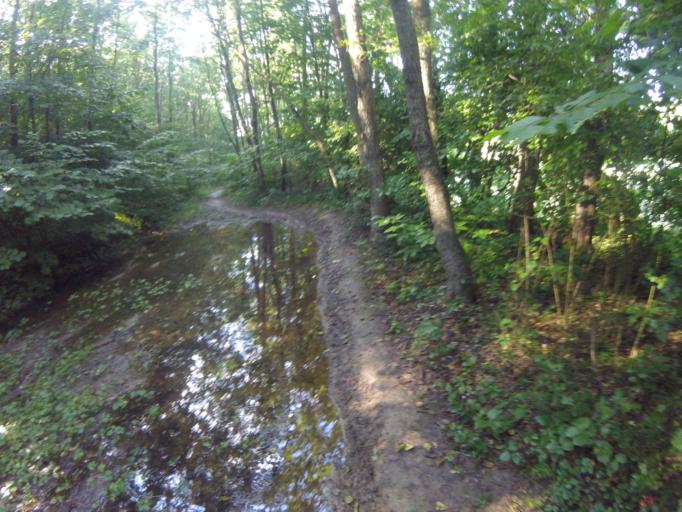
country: HU
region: Zala
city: Becsehely
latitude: 46.4964
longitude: 16.7394
